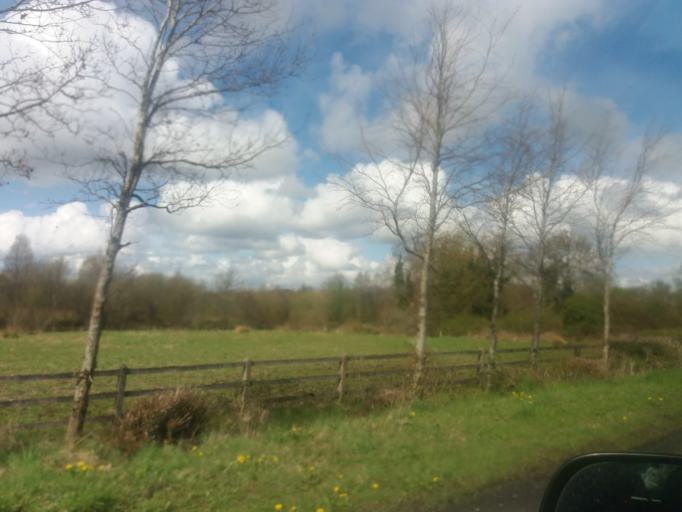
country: IE
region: Ulster
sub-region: An Cabhan
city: Belturbet
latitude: 54.1033
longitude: -7.4650
